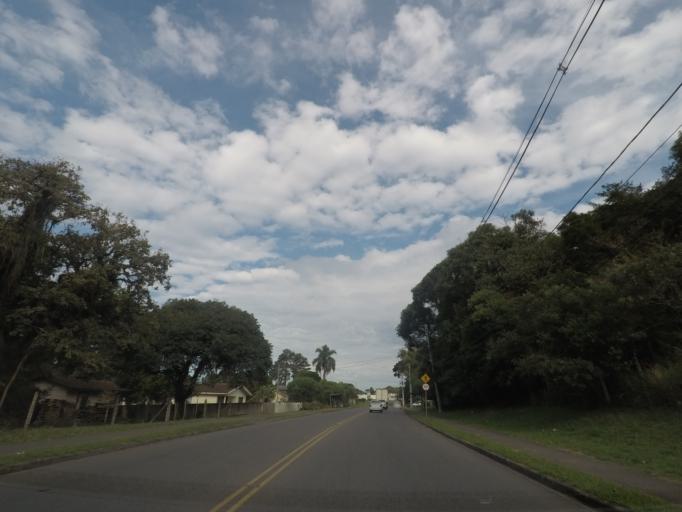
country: BR
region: Parana
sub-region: Sao Jose Dos Pinhais
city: Sao Jose dos Pinhais
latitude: -25.5560
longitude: -49.2929
